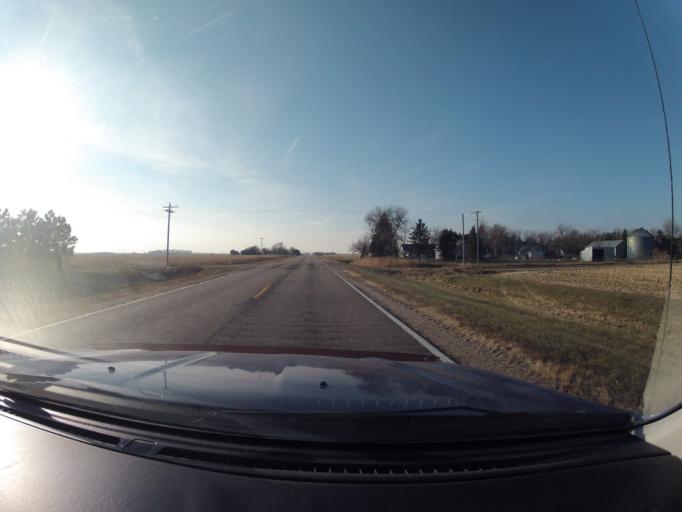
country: US
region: Nebraska
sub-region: Buffalo County
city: Kearney
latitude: 40.6410
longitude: -99.0366
